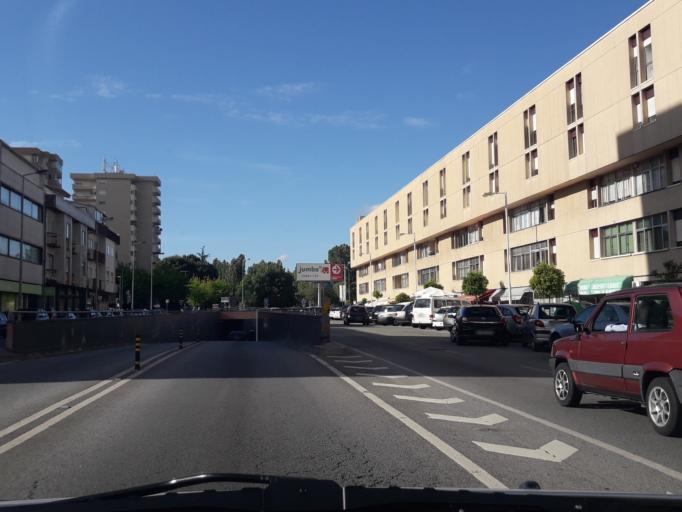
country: PT
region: Braga
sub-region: Vila Nova de Famalicao
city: Vila Nova de Famalicao
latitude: 41.4080
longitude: -8.5166
